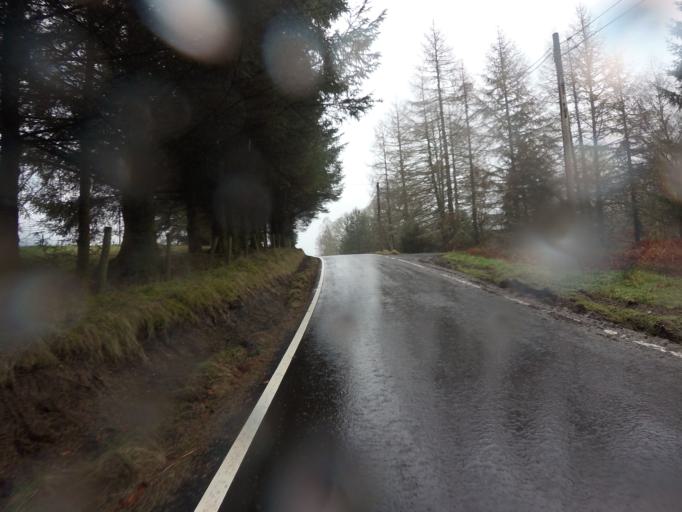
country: GB
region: Scotland
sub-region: Stirling
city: Killearn
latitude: 56.1909
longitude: -4.5035
